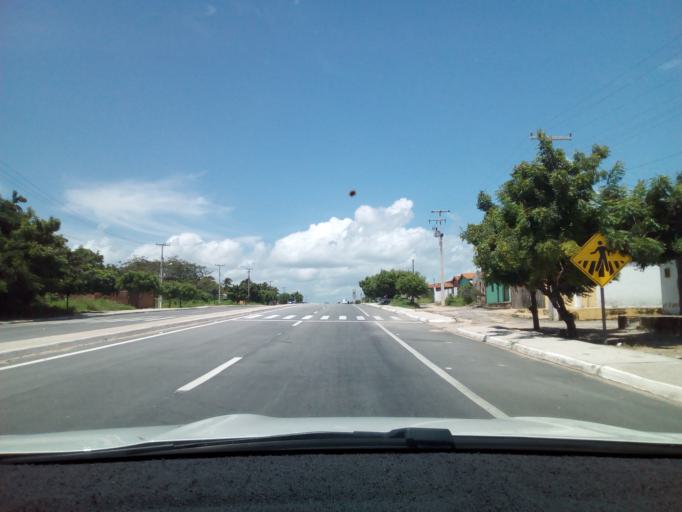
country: BR
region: Ceara
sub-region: Aracati
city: Aracati
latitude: -4.4696
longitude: -37.8013
